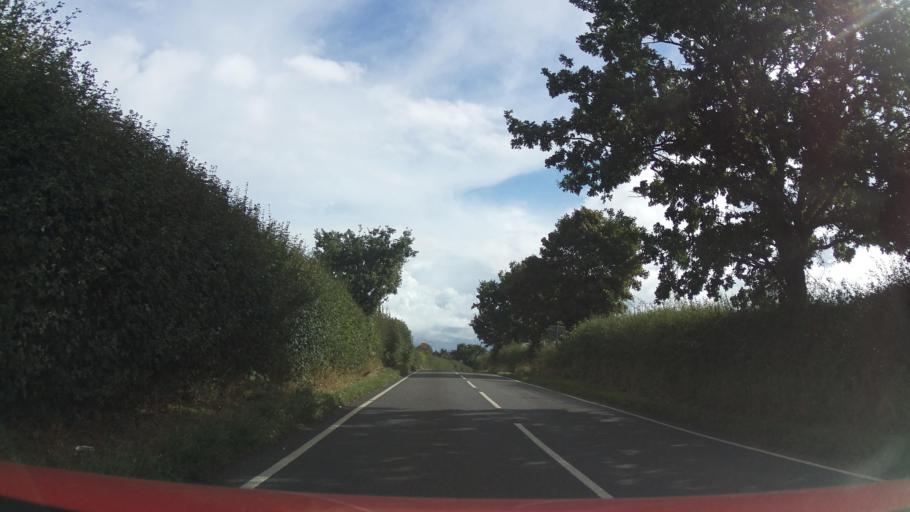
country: GB
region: England
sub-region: Telford and Wrekin
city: Madeley
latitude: 52.6328
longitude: -2.4136
